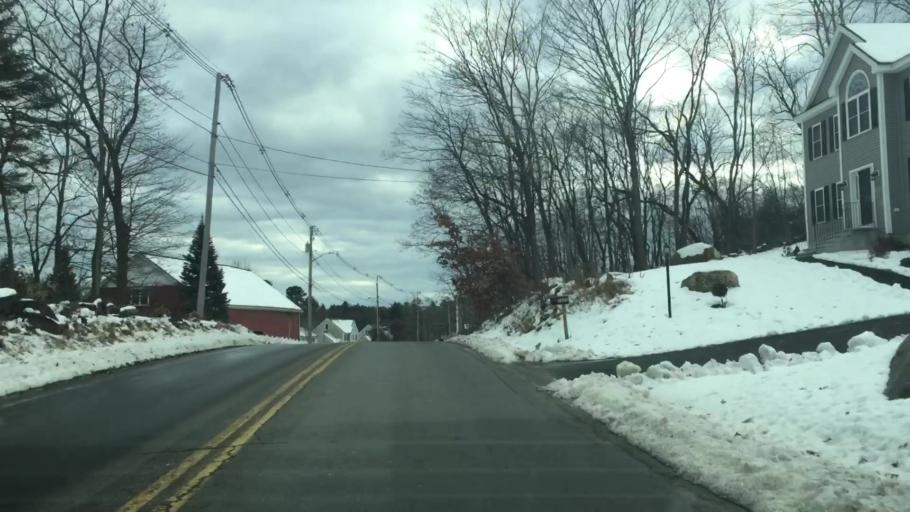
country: US
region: New Hampshire
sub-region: Hillsborough County
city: Pelham
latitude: 42.6973
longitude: -71.3513
